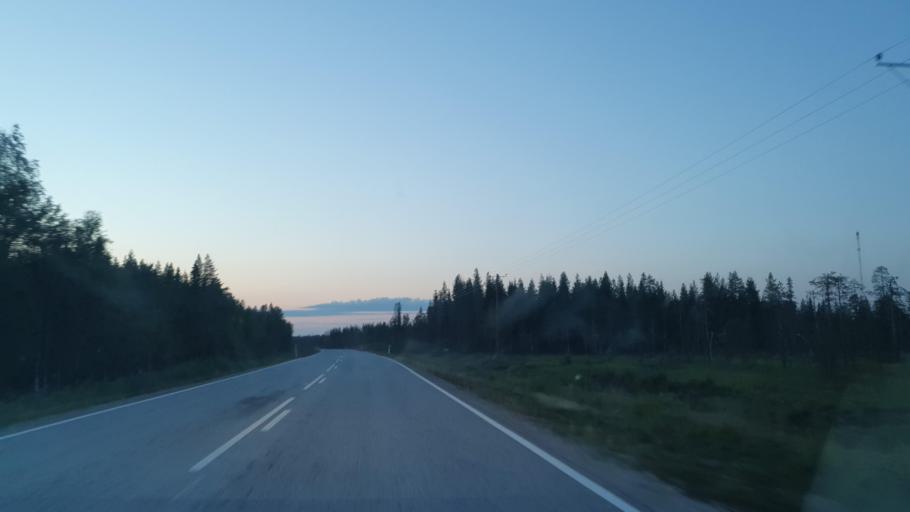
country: FI
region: Kainuu
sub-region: Kehys-Kainuu
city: Suomussalmi
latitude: 65.2497
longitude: 29.0198
